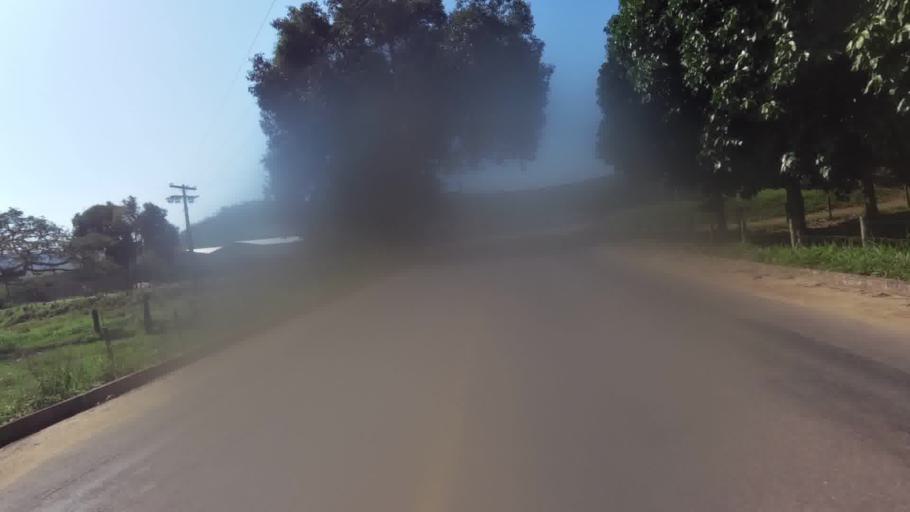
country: BR
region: Espirito Santo
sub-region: Alfredo Chaves
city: Alfredo Chaves
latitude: -20.6519
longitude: -40.7520
